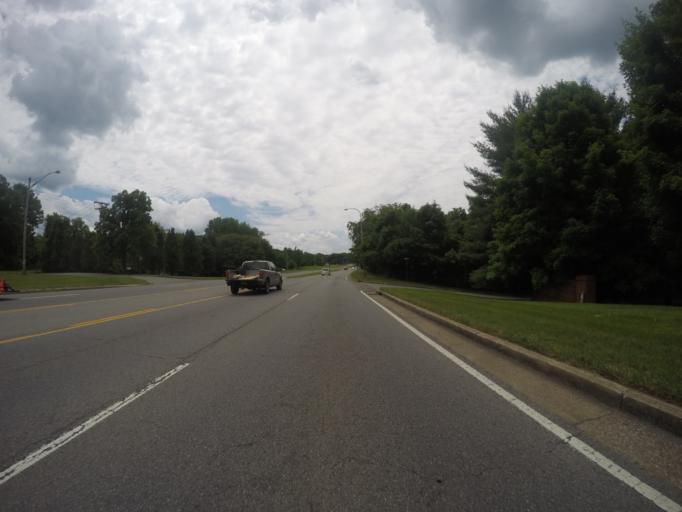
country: US
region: Tennessee
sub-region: Davidson County
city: Lakewood
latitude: 36.2141
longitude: -86.6230
